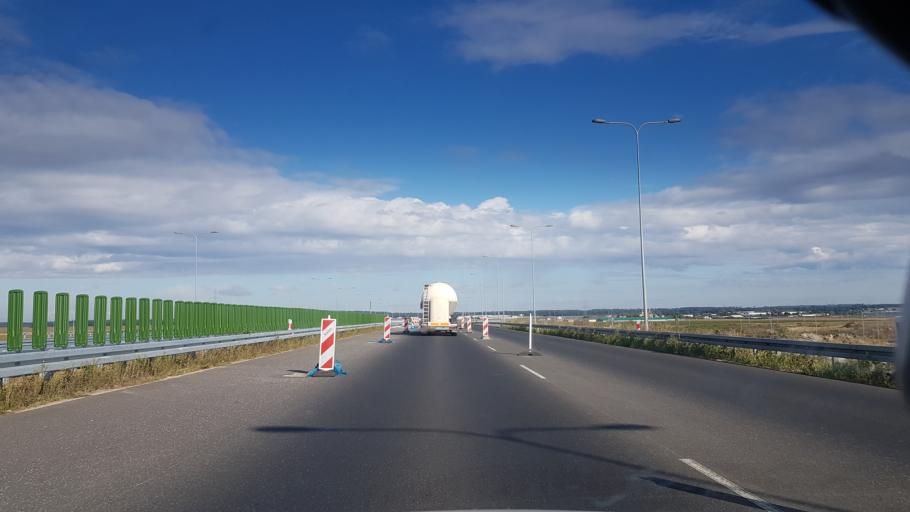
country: PL
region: Greater Poland Voivodeship
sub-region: Powiat poznanski
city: Steszew
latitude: 52.2657
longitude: 16.6681
